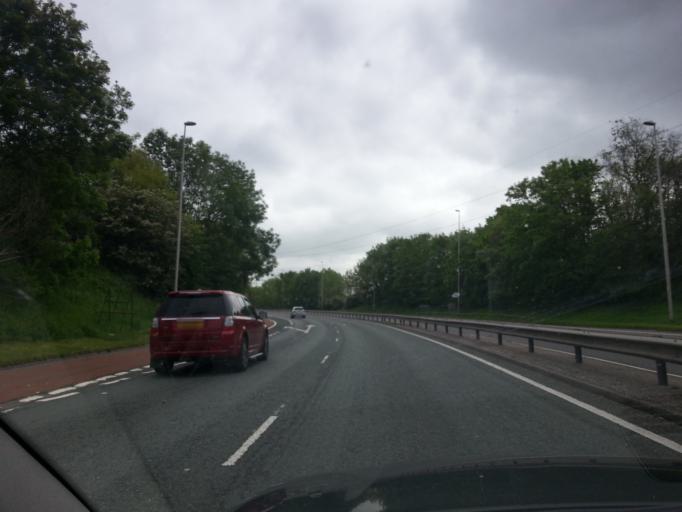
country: GB
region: England
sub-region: Borough of Halton
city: Runcorn
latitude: 53.3175
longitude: -2.7400
